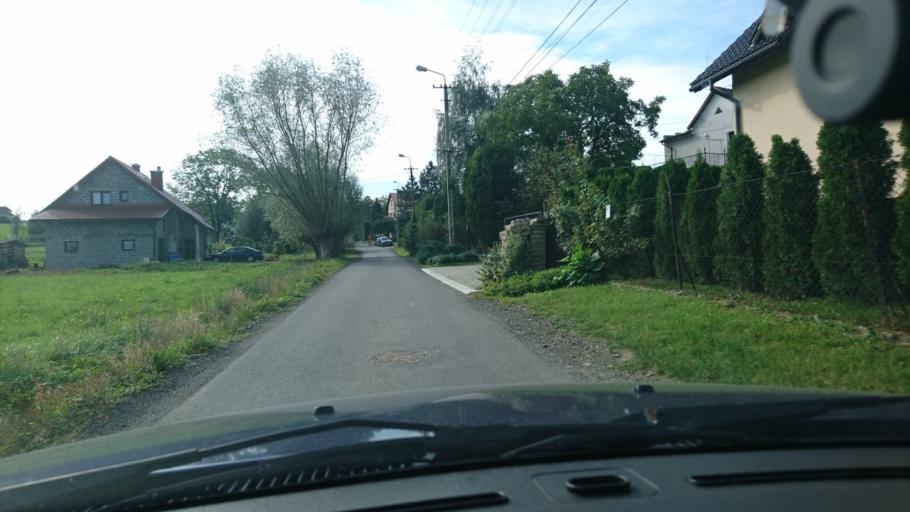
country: PL
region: Silesian Voivodeship
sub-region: Powiat bielski
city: Mazancowice
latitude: 49.8190
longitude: 18.9852
